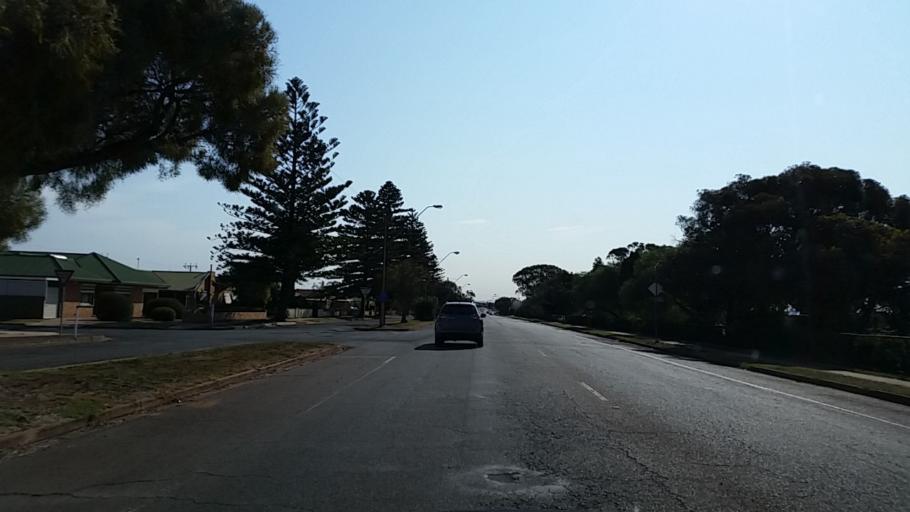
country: AU
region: South Australia
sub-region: Whyalla
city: Whyalla
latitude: -33.0408
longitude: 137.5683
